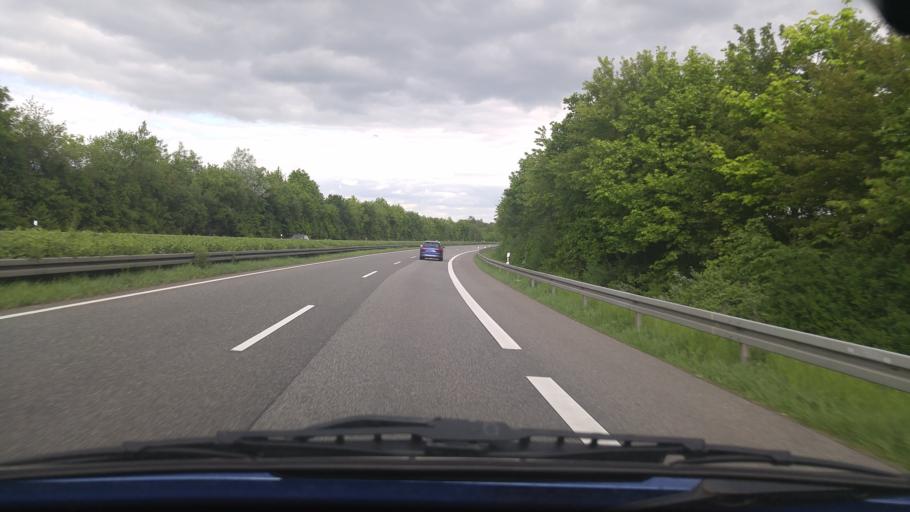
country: DE
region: Hesse
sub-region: Regierungsbezirk Darmstadt
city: Bad Vilbel
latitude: 50.1801
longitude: 8.7118
